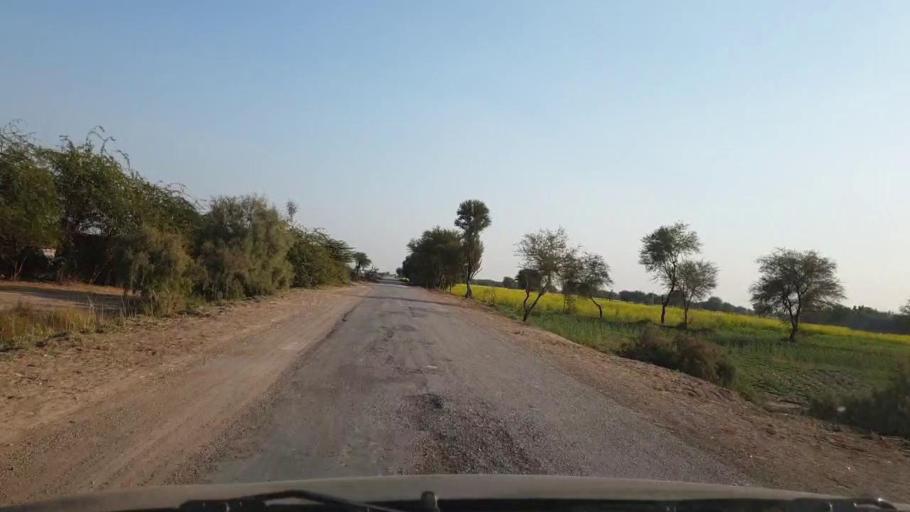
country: PK
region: Sindh
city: Jhol
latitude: 25.9496
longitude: 68.9028
